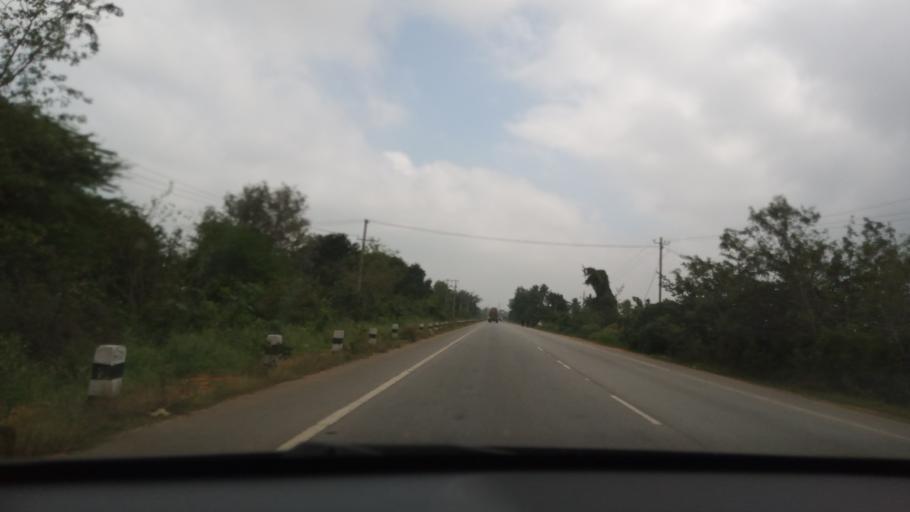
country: IN
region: Karnataka
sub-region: Chikkaballapur
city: Chintamani
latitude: 13.3642
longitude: 78.0479
